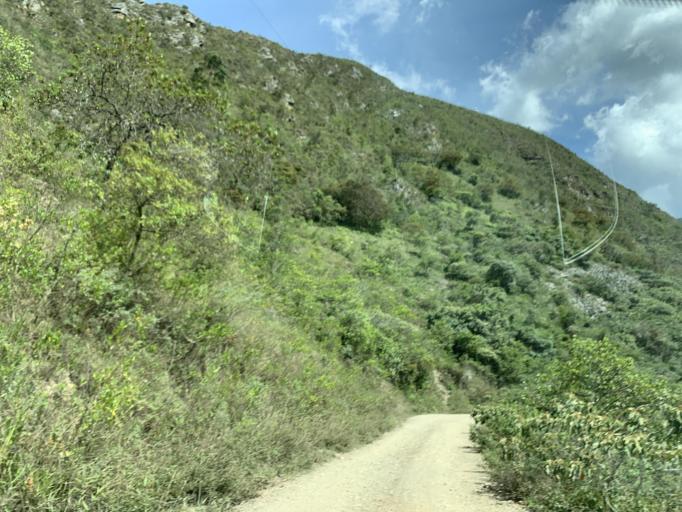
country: CO
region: Boyaca
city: Tipacoque
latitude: 6.4487
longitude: -72.7092
